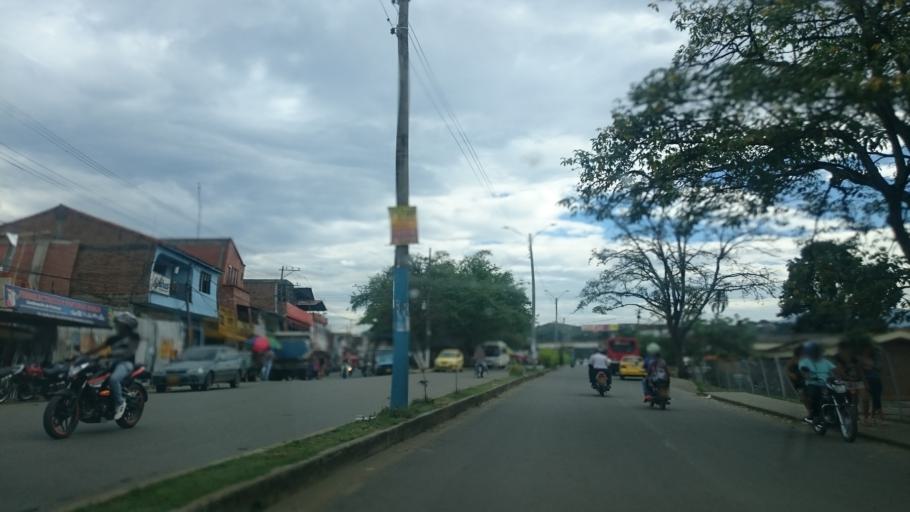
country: CO
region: Cauca
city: Santander de Quilichao
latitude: 3.0096
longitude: -76.4850
